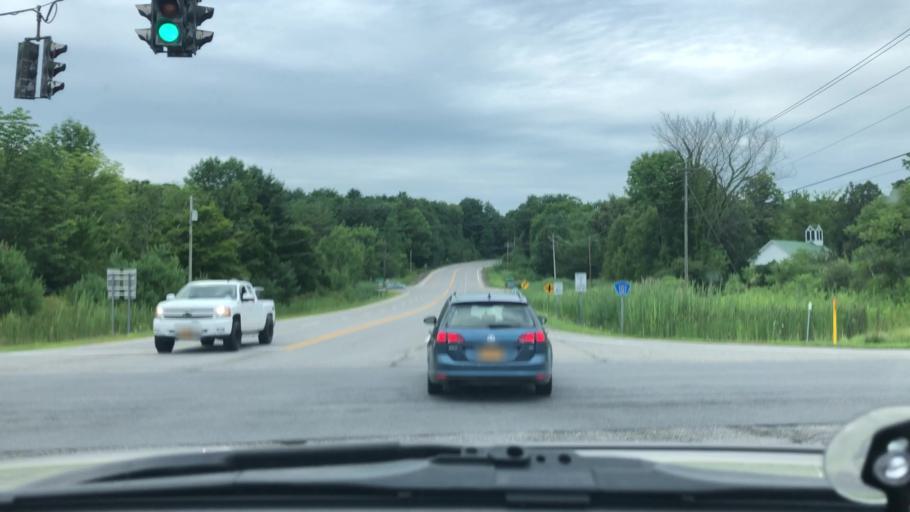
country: US
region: New York
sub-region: Saratoga County
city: Saratoga Springs
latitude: 43.1792
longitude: -73.7466
